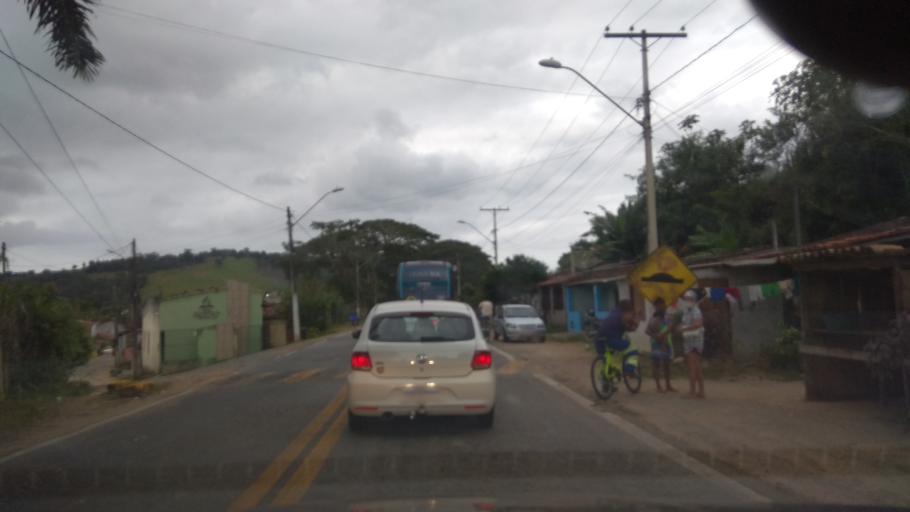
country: BR
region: Bahia
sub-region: Ubata
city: Ubata
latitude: -14.1981
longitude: -39.5389
